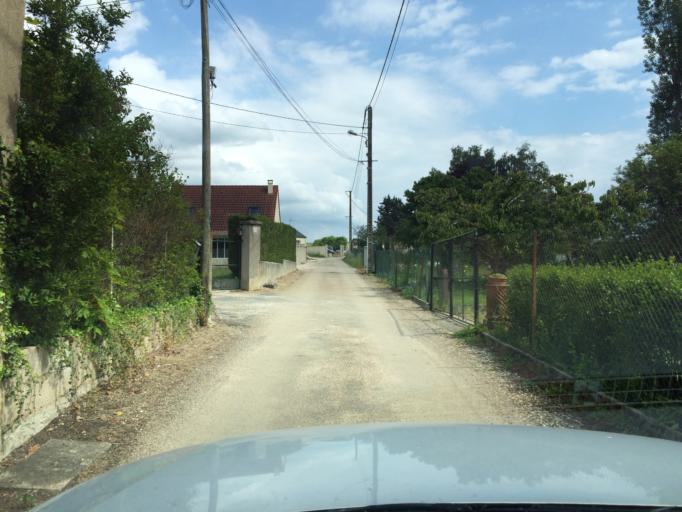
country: FR
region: Bourgogne
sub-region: Departement de l'Yonne
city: Fleury-la-Vallee
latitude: 47.8945
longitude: 3.4418
